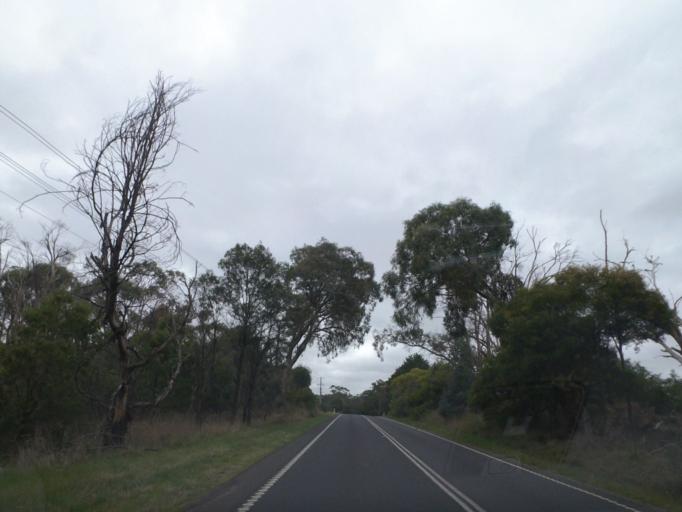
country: AU
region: Victoria
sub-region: Whittlesea
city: Whittlesea
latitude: -37.3818
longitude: 145.0300
